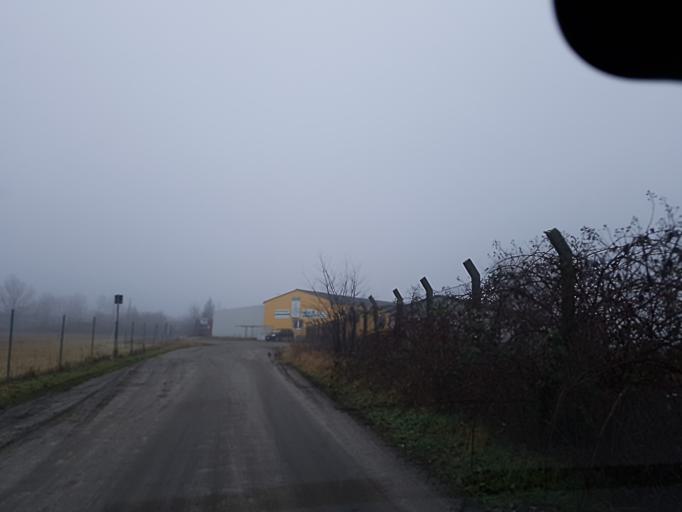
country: DE
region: Brandenburg
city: Finsterwalde
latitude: 51.6425
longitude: 13.7181
